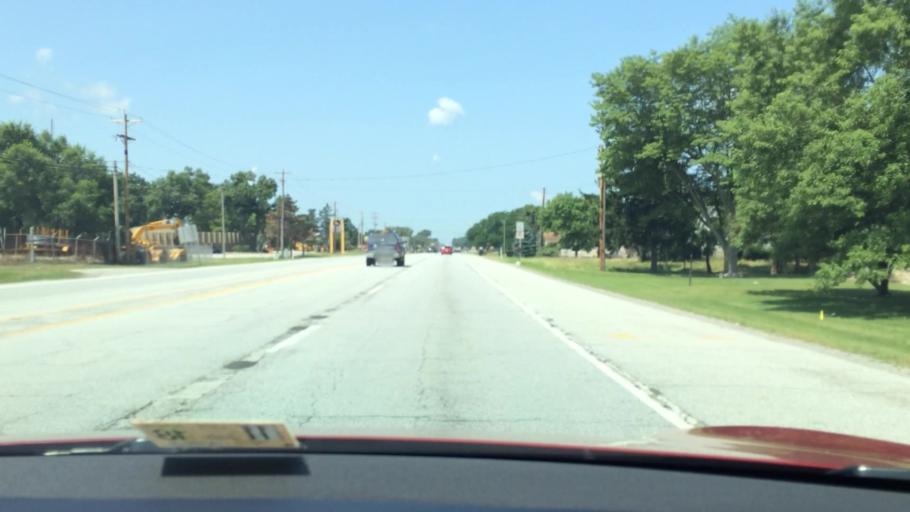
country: US
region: Indiana
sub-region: Saint Joseph County
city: South Bend
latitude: 41.6718
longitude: -86.3515
